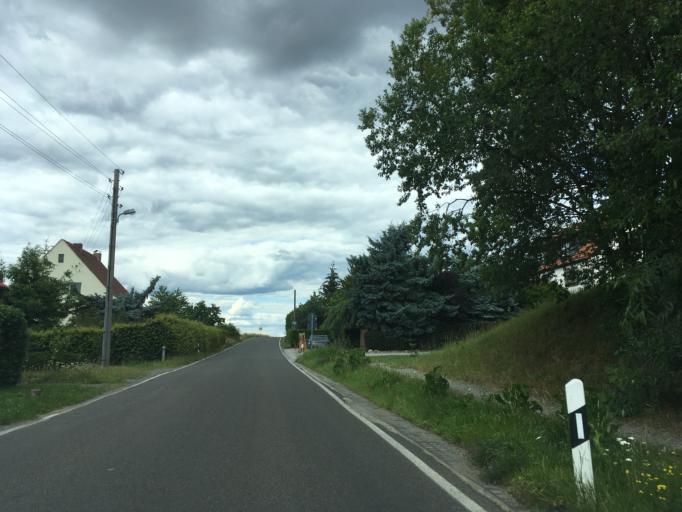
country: DE
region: Saxony
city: Wachau
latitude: 51.1418
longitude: 13.9142
